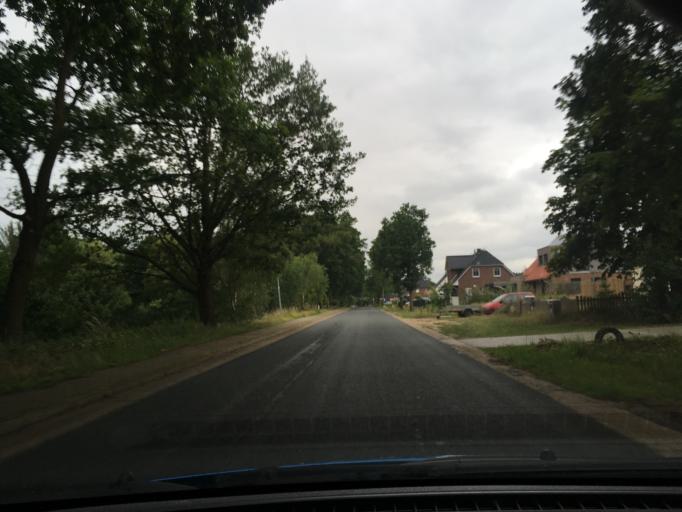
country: DE
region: Lower Saxony
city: Soderstorf
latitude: 53.1434
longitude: 10.1592
